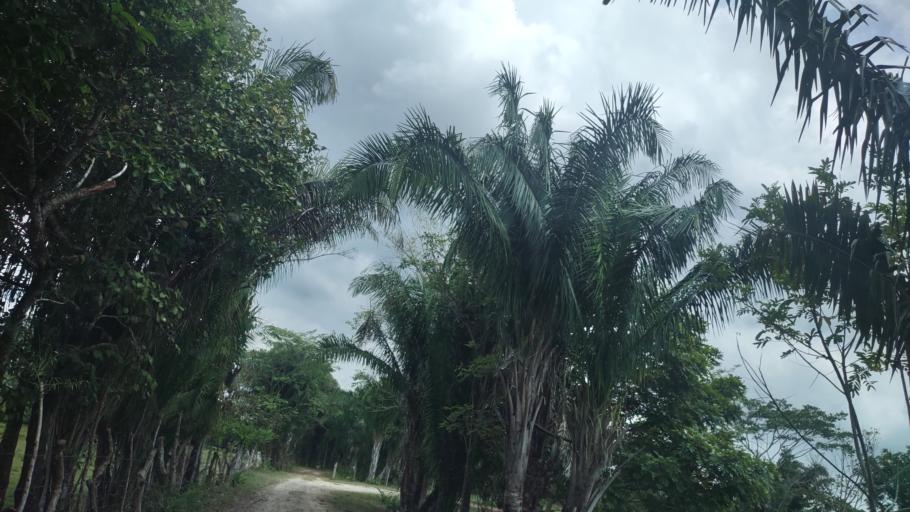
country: MX
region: Veracruz
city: Las Choapas
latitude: 17.9652
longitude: -94.1252
